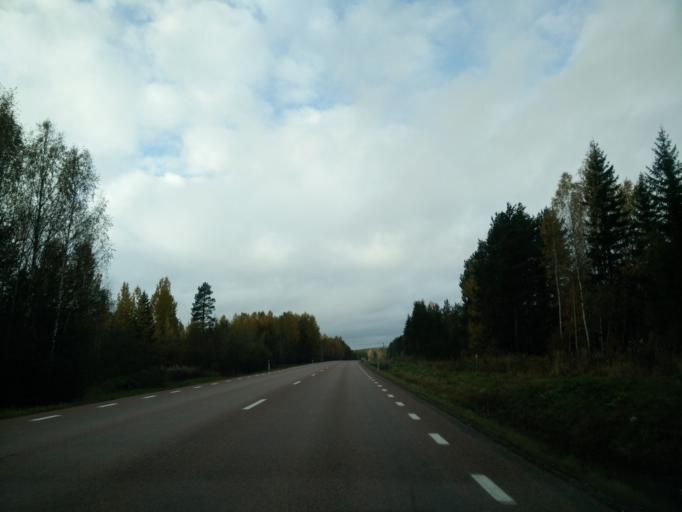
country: SE
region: Vaesternorrland
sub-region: Ange Kommun
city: Ange
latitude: 62.5177
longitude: 15.6035
